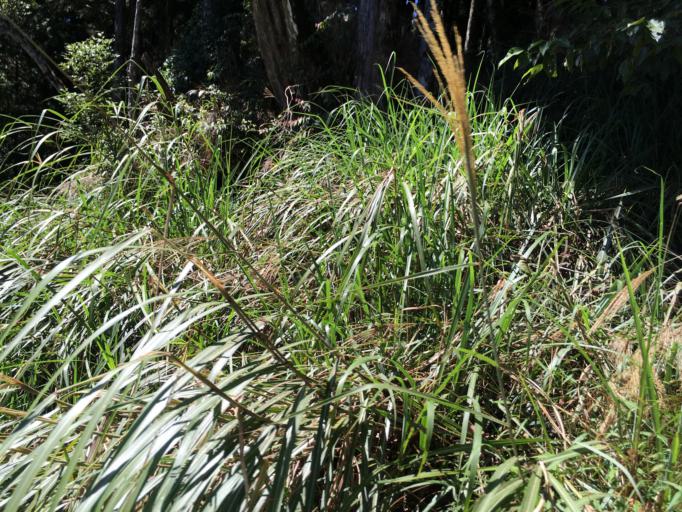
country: TW
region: Taiwan
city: Daxi
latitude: 24.5299
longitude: 121.4019
